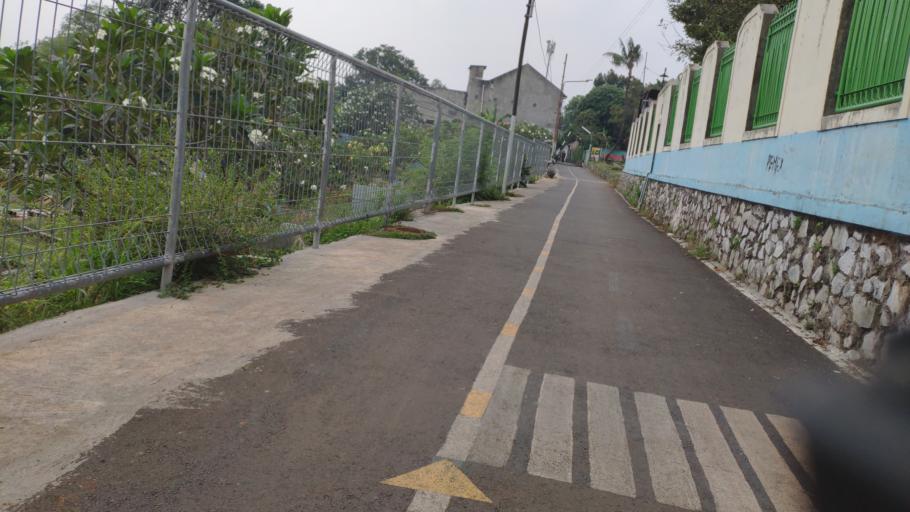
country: ID
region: Jakarta Raya
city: Jakarta
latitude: -6.3006
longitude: 106.8273
